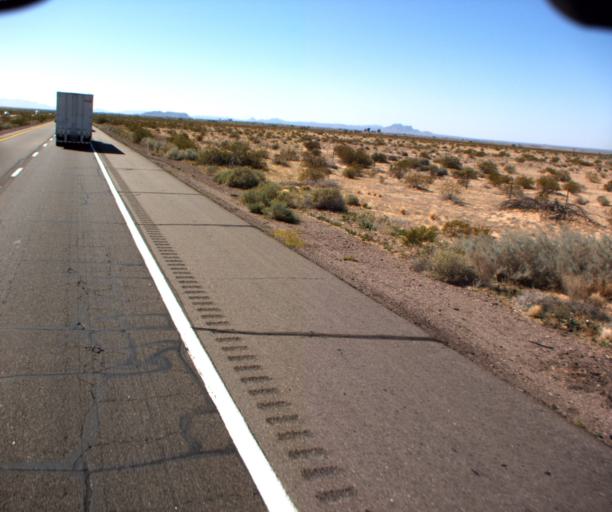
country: US
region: Arizona
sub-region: Yuma County
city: Wellton
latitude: 32.7118
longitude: -113.8344
